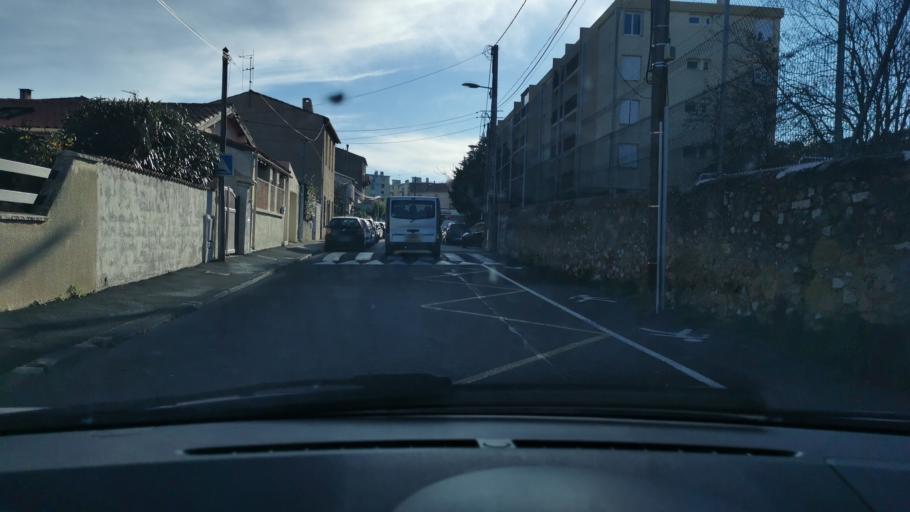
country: FR
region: Languedoc-Roussillon
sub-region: Departement de l'Herault
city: Sete
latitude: 43.4116
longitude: 3.6761
